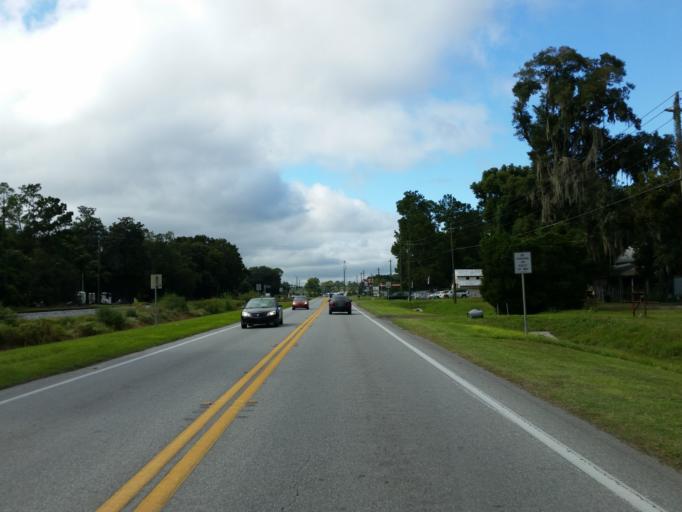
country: US
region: Florida
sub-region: Columbia County
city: Watertown
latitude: 30.1817
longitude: -82.5970
